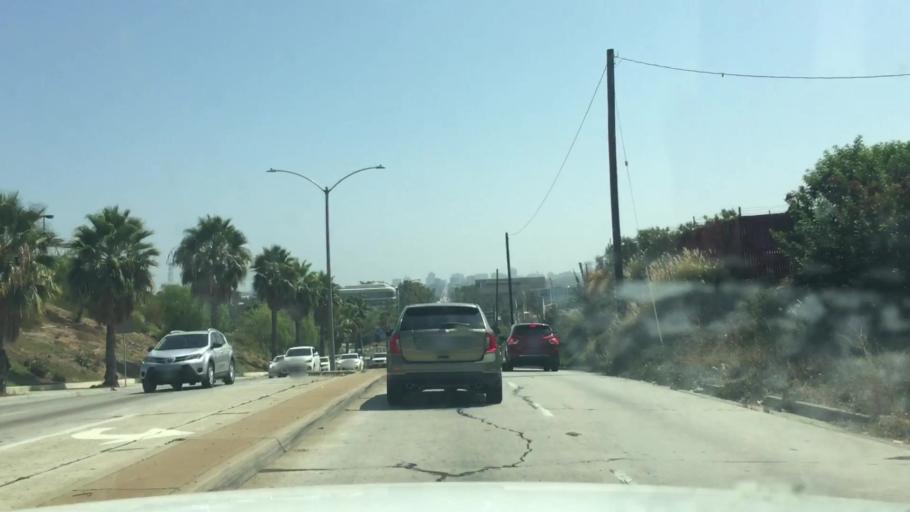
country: US
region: California
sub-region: Los Angeles County
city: Signal Hill
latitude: 33.8132
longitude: -118.1851
